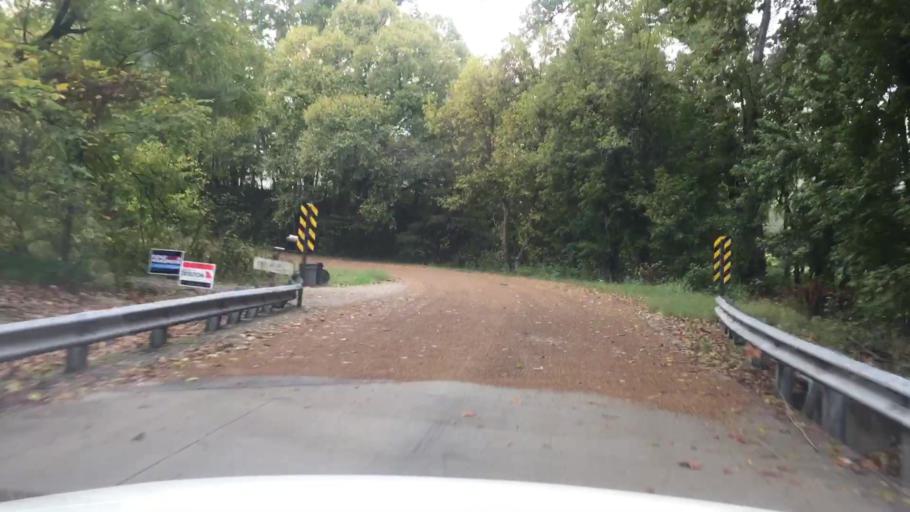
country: US
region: Missouri
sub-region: Boone County
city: Ashland
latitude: 38.8225
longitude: -92.3289
